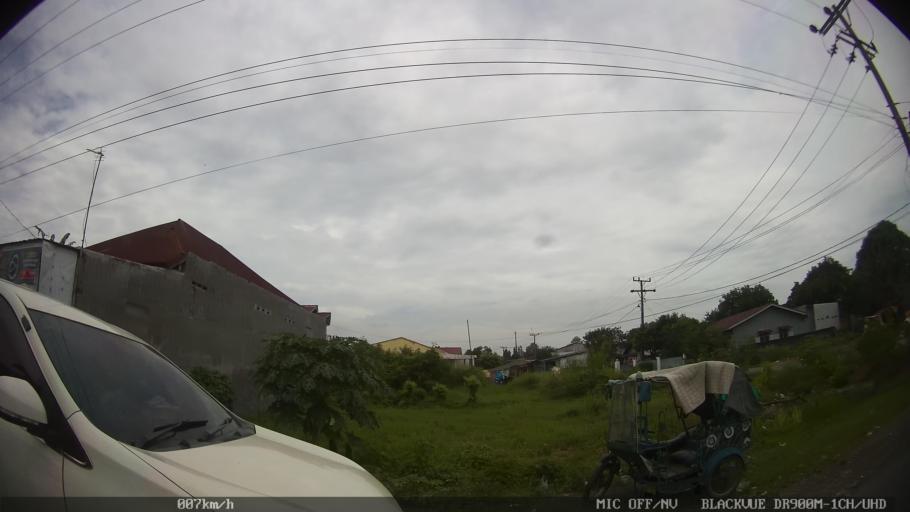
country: ID
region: North Sumatra
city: Sunggal
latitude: 3.6141
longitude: 98.6003
